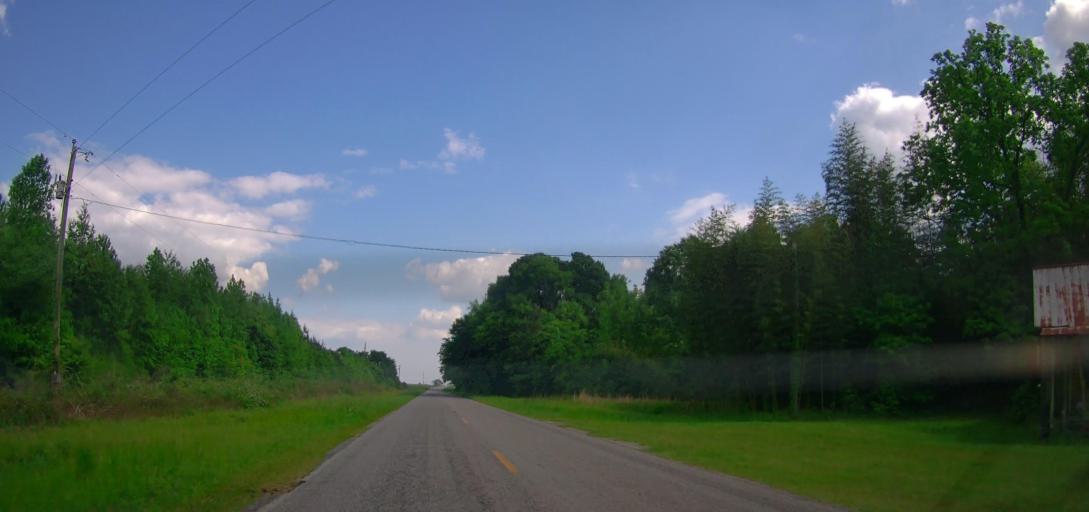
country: US
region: Georgia
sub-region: Laurens County
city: East Dublin
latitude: 32.6901
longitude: -82.8991
